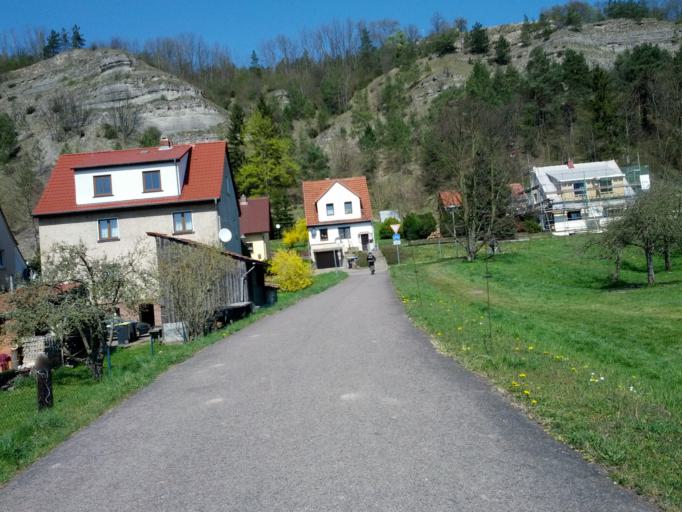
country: DE
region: Thuringia
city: Thal
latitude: 50.9595
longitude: 10.3910
